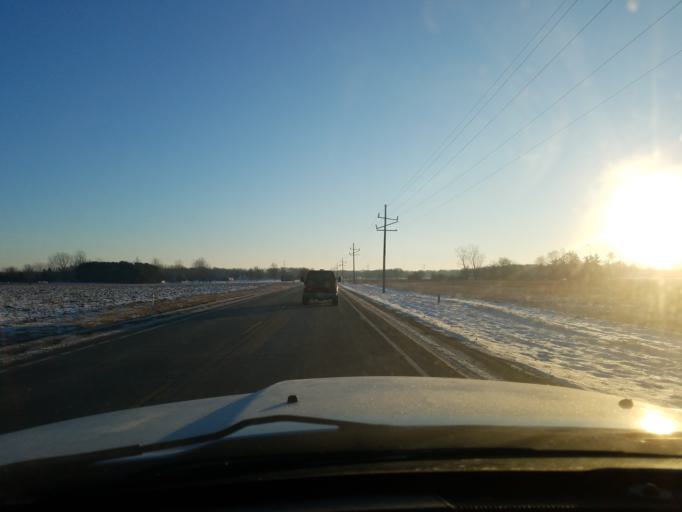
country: US
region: Indiana
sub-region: Marshall County
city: Bremen
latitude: 41.4537
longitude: -86.1094
